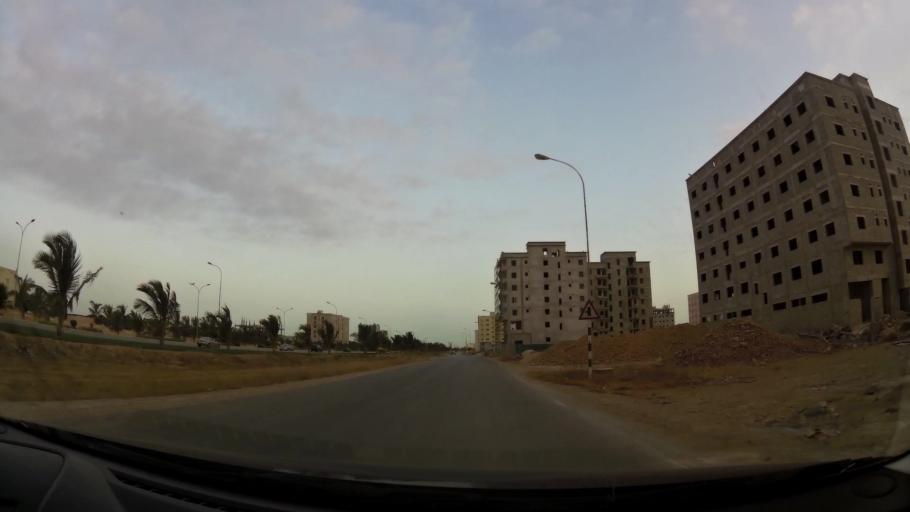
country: OM
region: Zufar
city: Salalah
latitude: 17.0270
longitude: 54.0313
